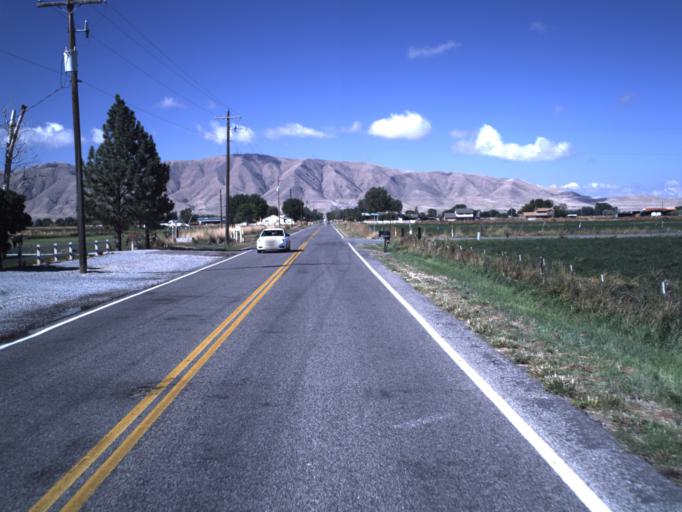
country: US
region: Utah
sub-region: Utah County
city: Benjamin
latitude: 40.0983
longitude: -111.7107
